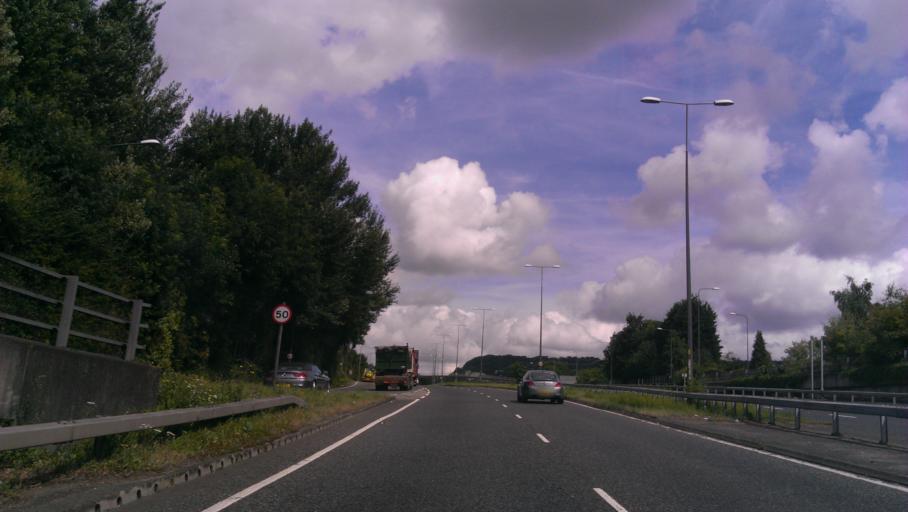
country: GB
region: England
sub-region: Kent
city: Boxley
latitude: 51.3020
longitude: 0.5133
